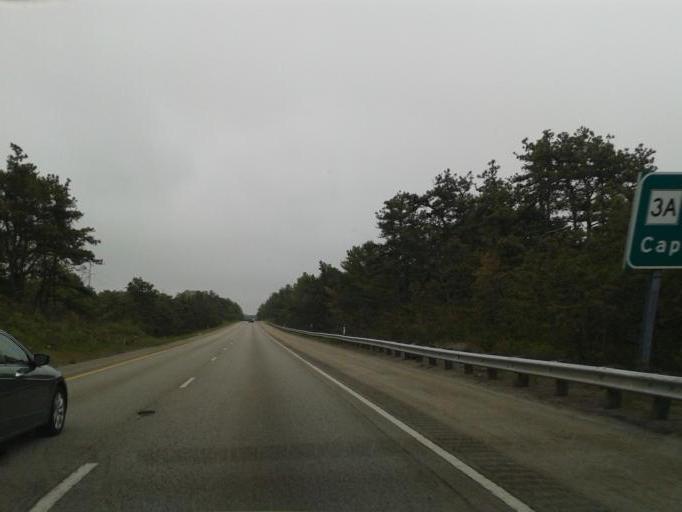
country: US
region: Massachusetts
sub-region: Plymouth County
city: White Island Shores
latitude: 41.8647
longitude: -70.5921
